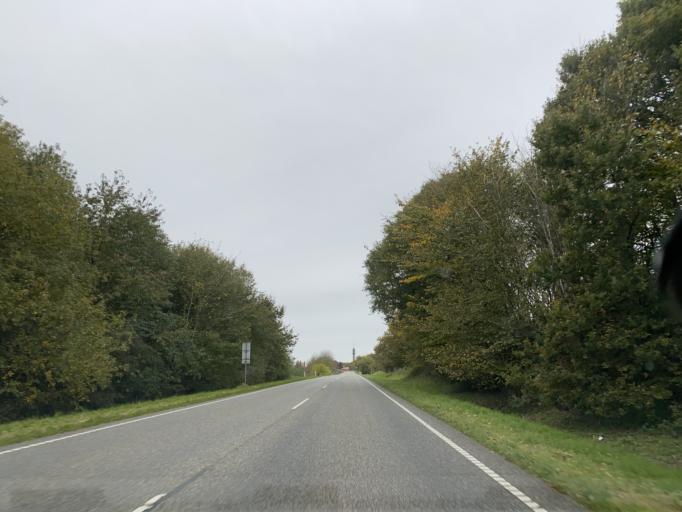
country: DK
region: Central Jutland
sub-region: Skanderborg Kommune
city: Ry
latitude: 56.1699
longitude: 9.8074
